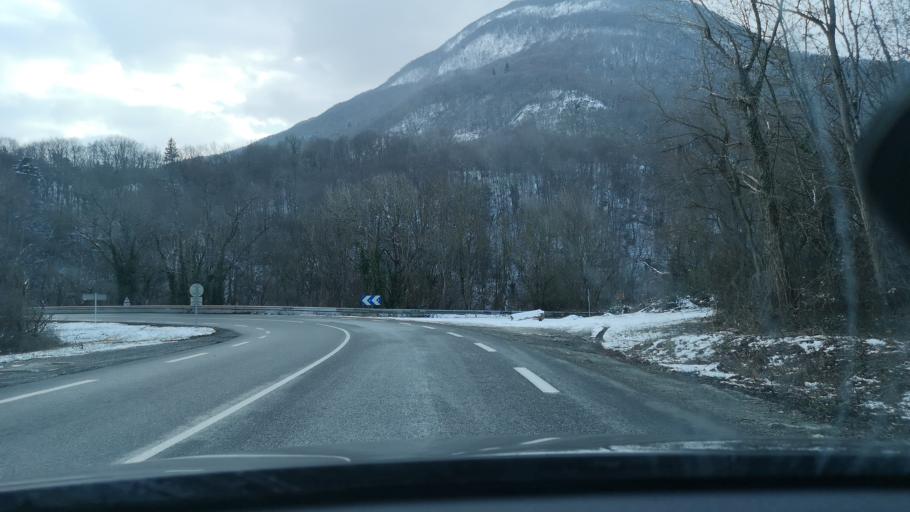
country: FR
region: Rhone-Alpes
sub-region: Departement de l'Ain
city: Collonges
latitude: 46.1213
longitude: 5.9033
